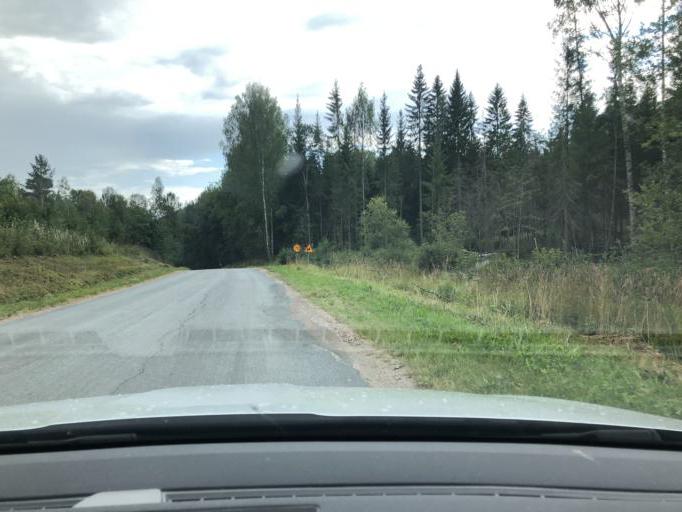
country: SE
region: Vaesternorrland
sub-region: Solleftea Kommun
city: Solleftea
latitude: 63.2134
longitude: 17.1983
